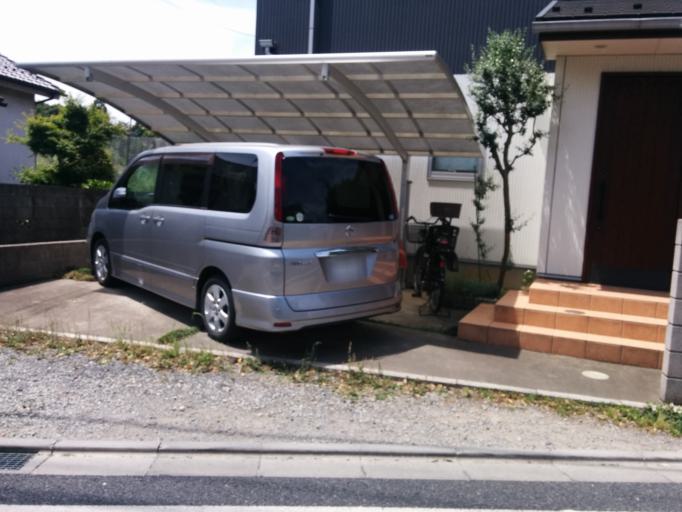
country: JP
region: Tokyo
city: Higashimurayama-shi
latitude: 35.7537
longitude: 139.4818
